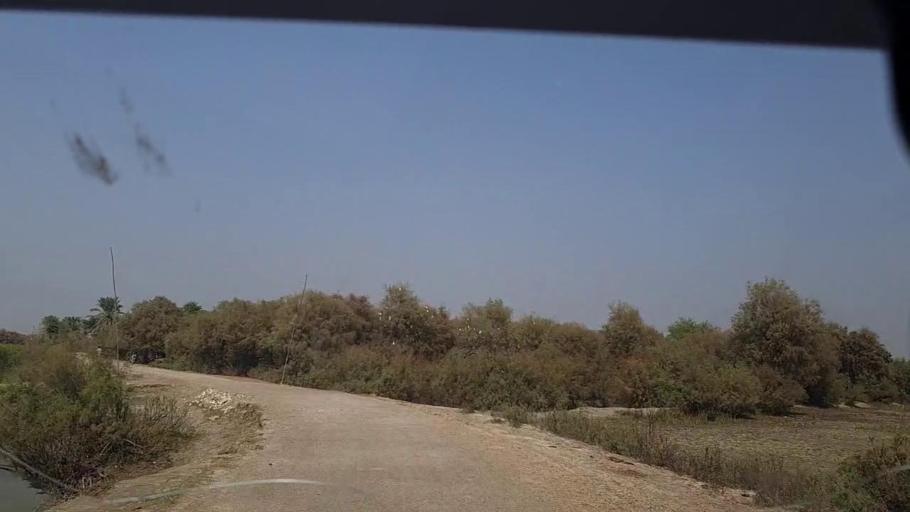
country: PK
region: Sindh
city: Shikarpur
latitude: 28.0887
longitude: 68.6696
